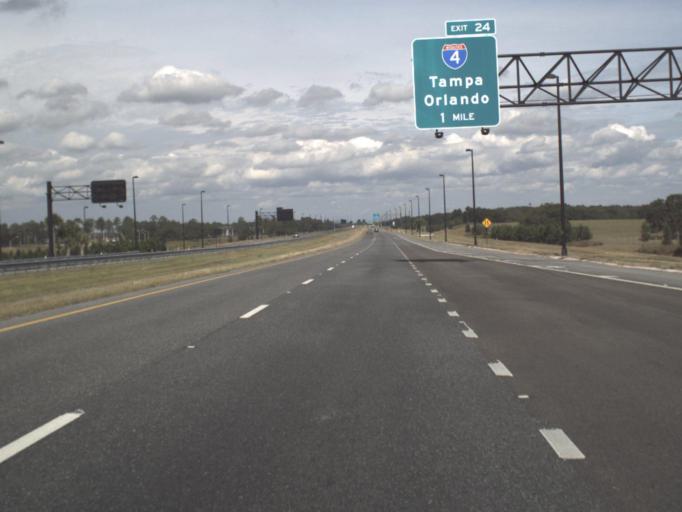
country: US
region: Florida
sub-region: Polk County
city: Polk City
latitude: 28.1373
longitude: -81.8406
